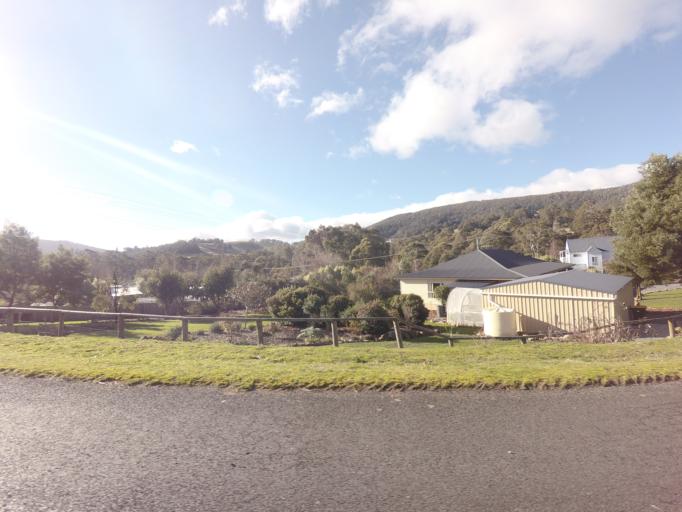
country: AU
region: Tasmania
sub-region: Glenorchy
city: Berriedale
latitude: -42.8424
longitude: 147.1890
